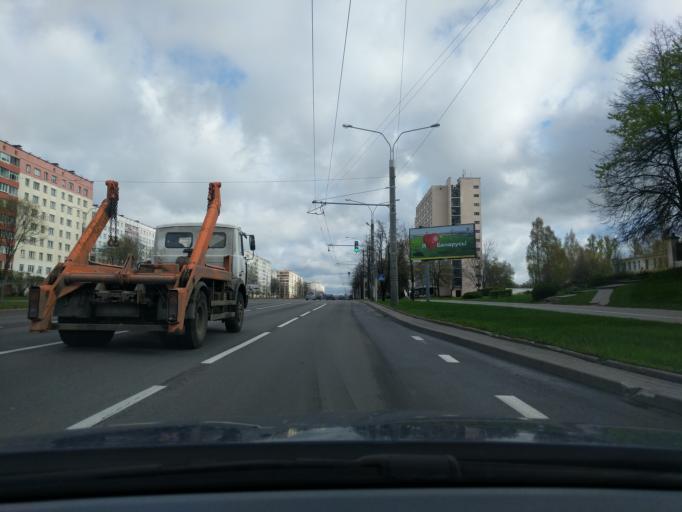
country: BY
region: Minsk
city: Novoye Medvezhino
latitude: 53.8961
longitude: 27.4976
